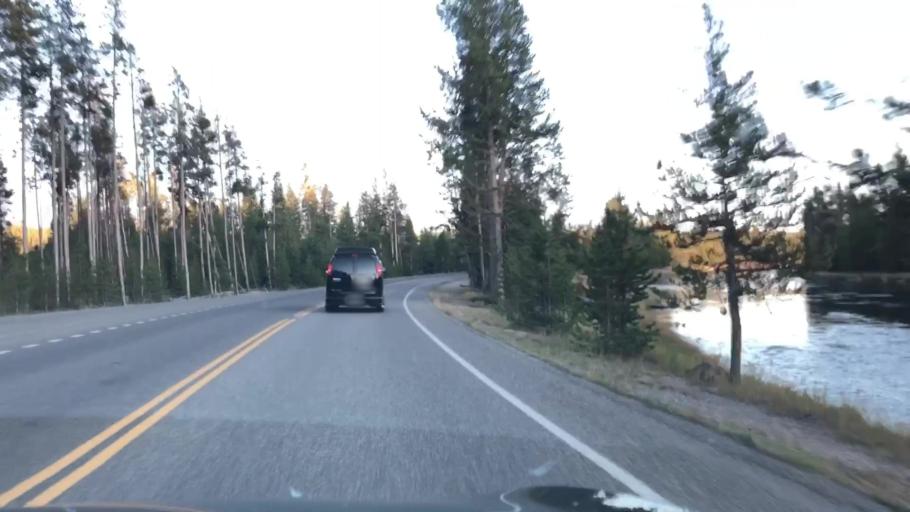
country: US
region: Montana
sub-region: Gallatin County
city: West Yellowstone
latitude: 44.6004
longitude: -110.8336
